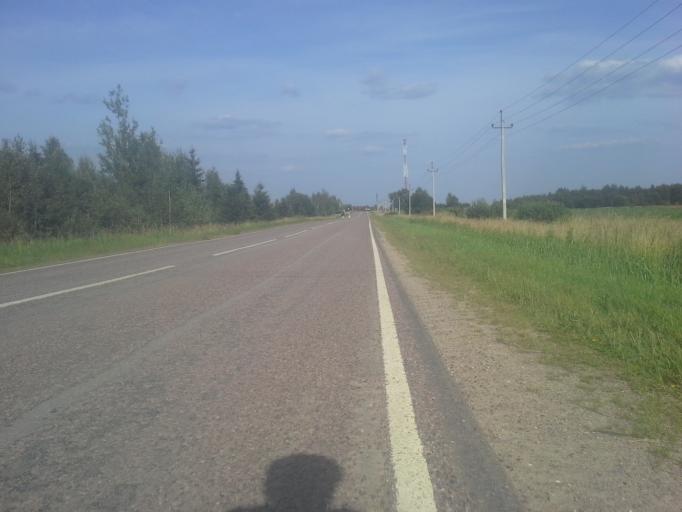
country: RU
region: Moskovskaya
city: Karinskoye
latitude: 55.7835
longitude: 36.6492
